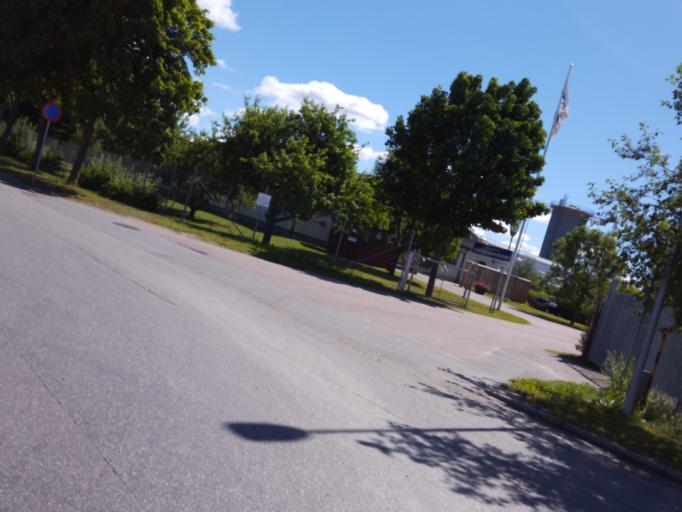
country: SE
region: Uppsala
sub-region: Uppsala Kommun
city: Uppsala
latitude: 59.8451
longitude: 17.6592
